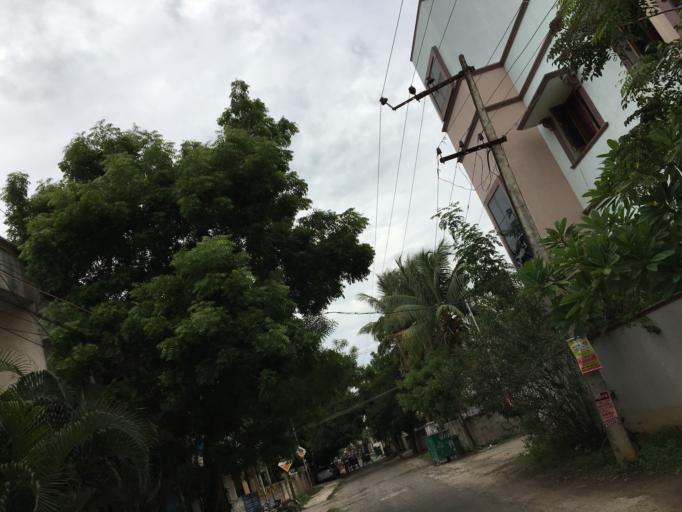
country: IN
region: Tamil Nadu
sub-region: Kancheepuram
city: Madipakkam
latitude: 12.9724
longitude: 80.2164
